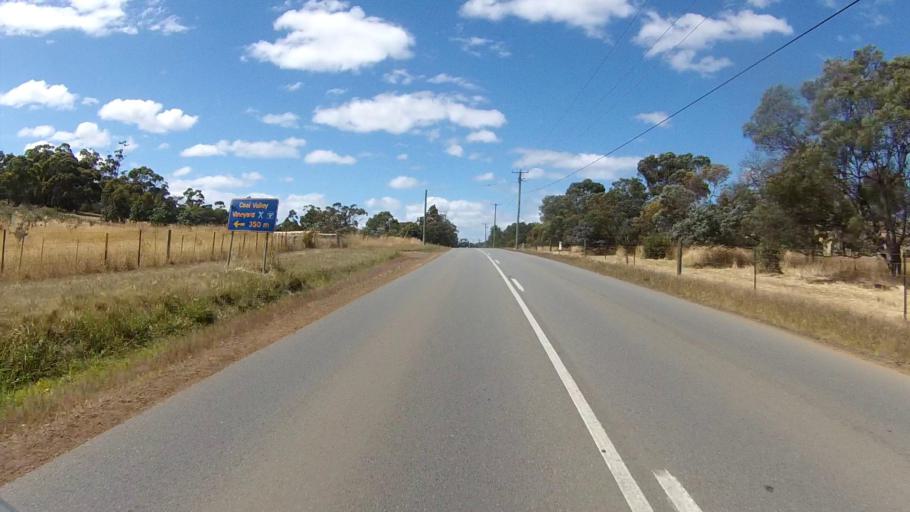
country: AU
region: Tasmania
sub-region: Clarence
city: Cambridge
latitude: -42.8204
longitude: 147.4413
